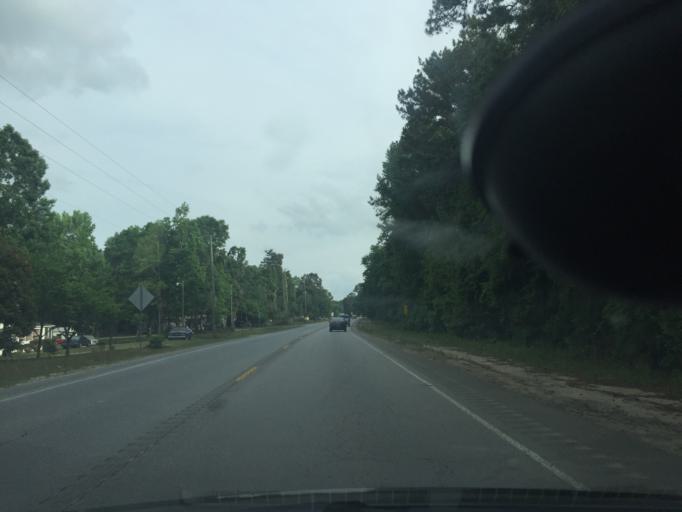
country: US
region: Georgia
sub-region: Bryan County
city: Richmond Hill
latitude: 32.0337
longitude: -81.3247
